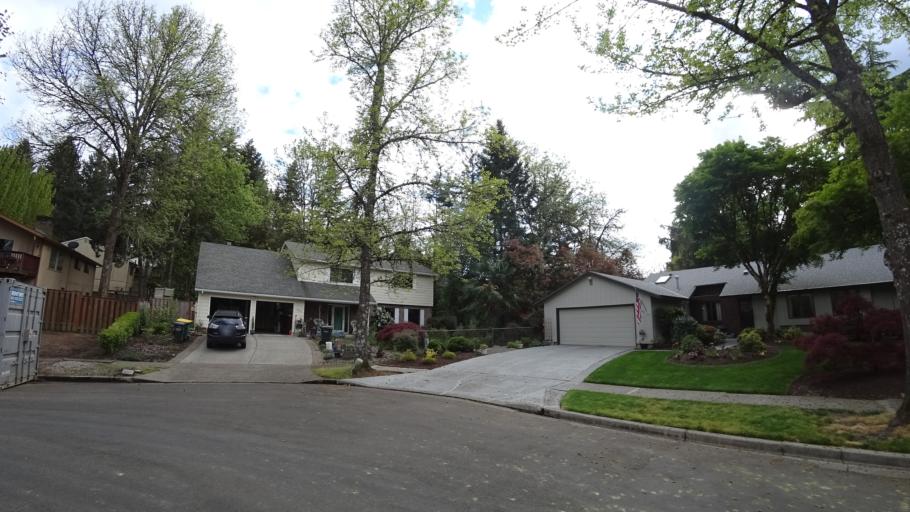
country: US
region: Oregon
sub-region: Washington County
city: Beaverton
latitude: 45.4523
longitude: -122.8198
